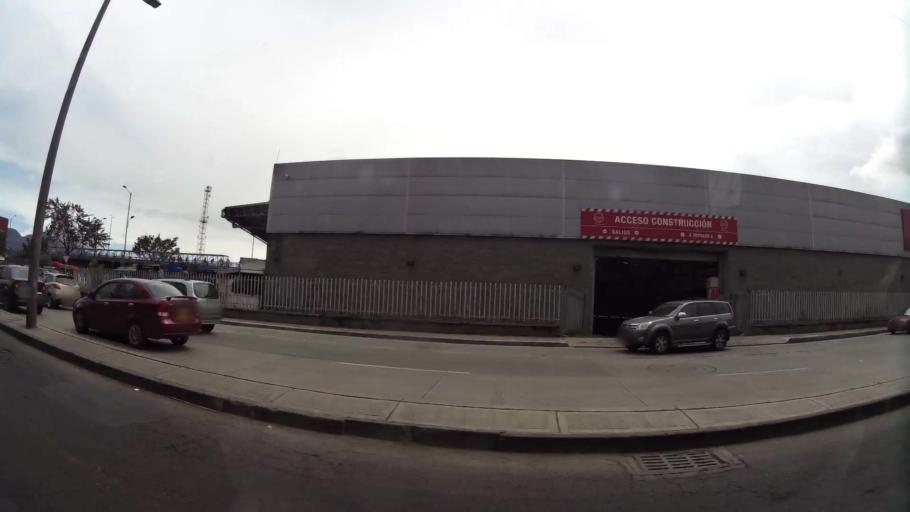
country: CO
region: Bogota D.C.
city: Bogota
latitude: 4.6303
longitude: -74.1224
